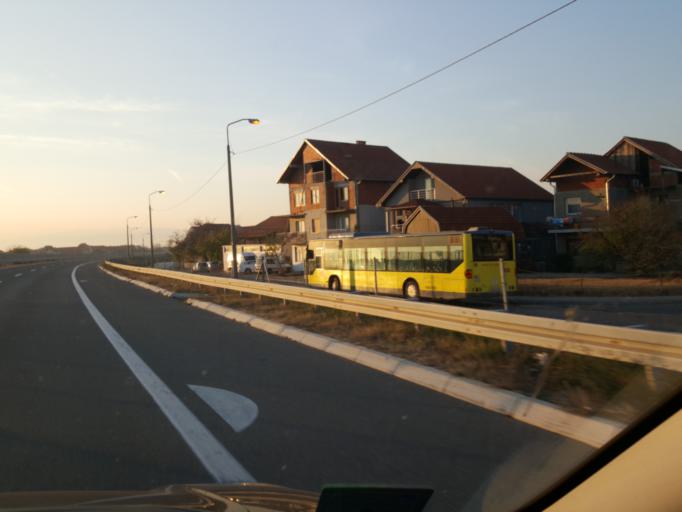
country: RS
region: Central Serbia
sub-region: Nisavski Okrug
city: Nis
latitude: 43.3422
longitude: 21.8888
